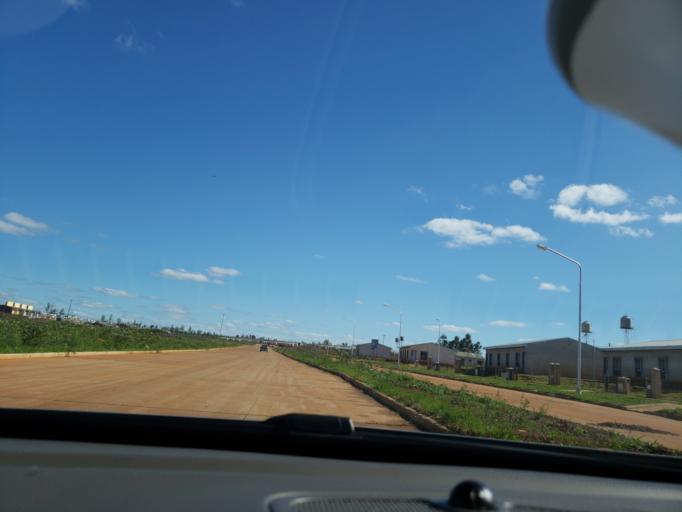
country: AR
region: Misiones
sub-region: Departamento de Capital
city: Posadas
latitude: -27.4050
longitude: -55.9886
